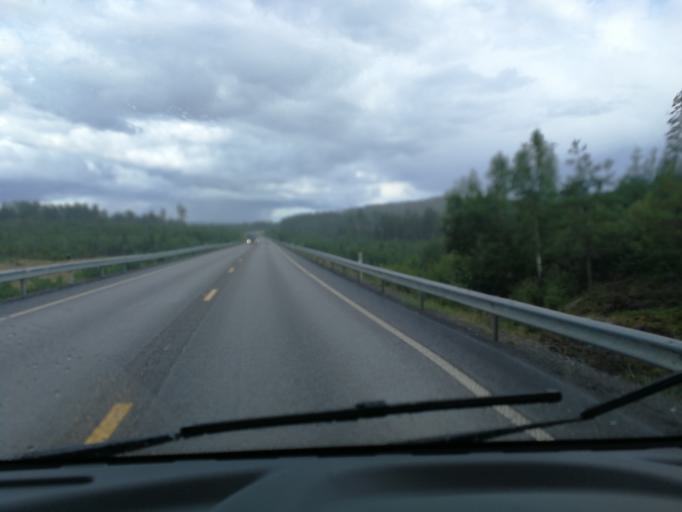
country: NO
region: Ostfold
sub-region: Marker
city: Orje
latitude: 59.5377
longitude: 11.5511
